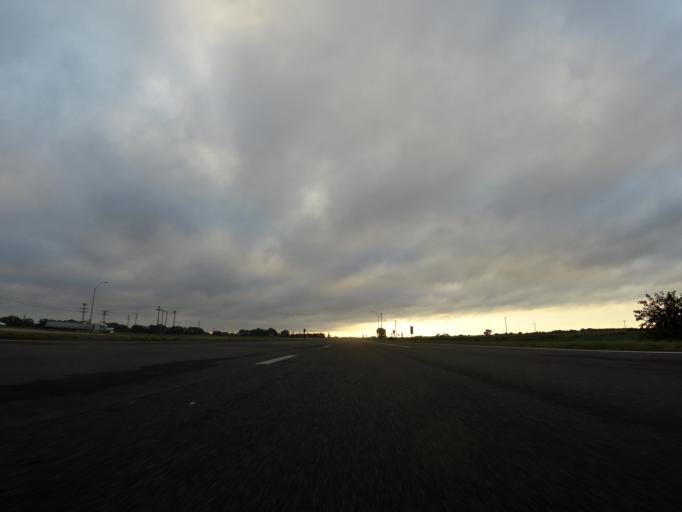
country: US
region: Kansas
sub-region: Sedgwick County
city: Colwich
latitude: 37.8245
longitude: -97.5203
